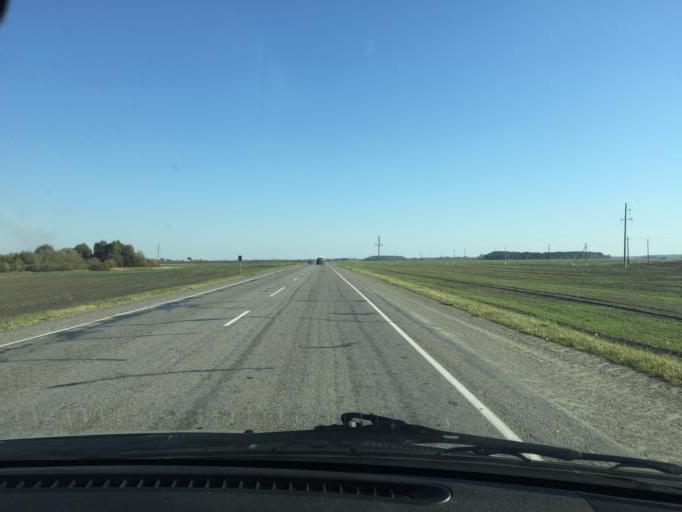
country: BY
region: Gomel
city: Turaw
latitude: 52.0623
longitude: 27.7871
